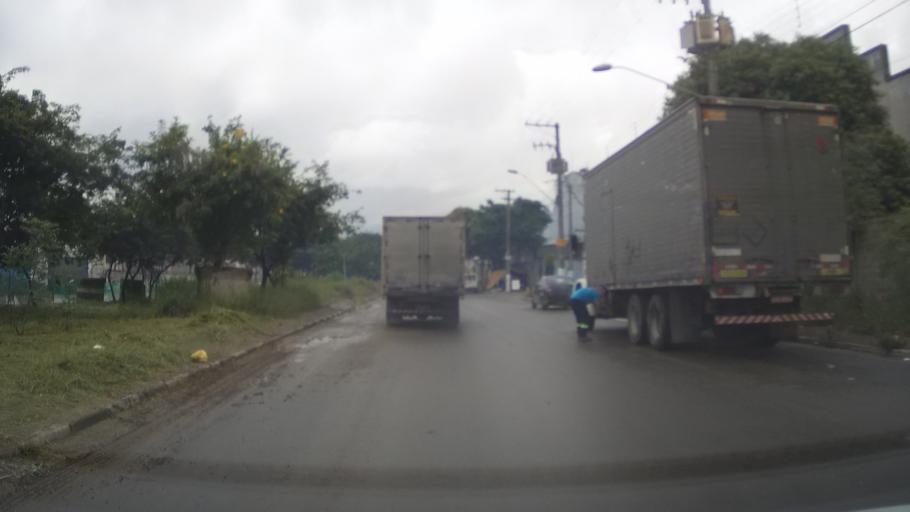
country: BR
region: Sao Paulo
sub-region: Guarulhos
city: Guarulhos
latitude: -23.4662
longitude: -46.4784
